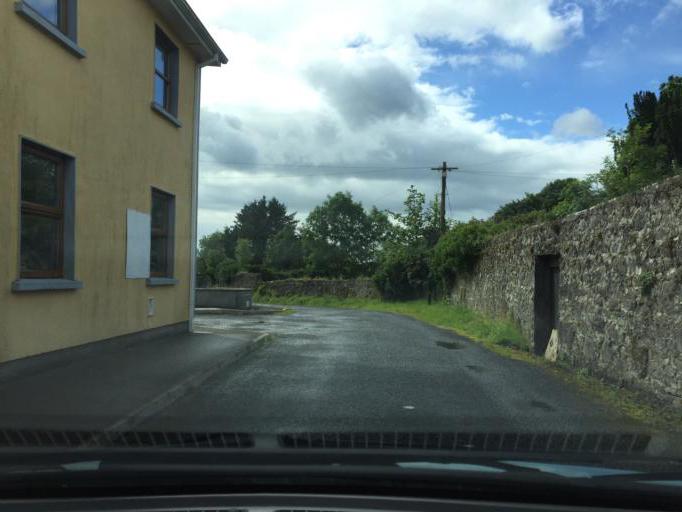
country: IE
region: Connaught
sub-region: Maigh Eo
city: Swinford
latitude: 54.0361
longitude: -8.8998
